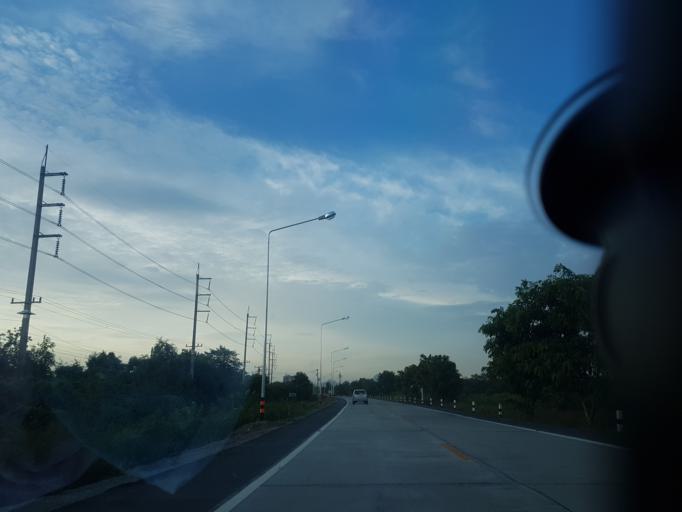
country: TH
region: Phra Nakhon Si Ayutthaya
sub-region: Amphoe Tha Ruea
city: Tha Ruea
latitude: 14.5483
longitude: 100.7617
